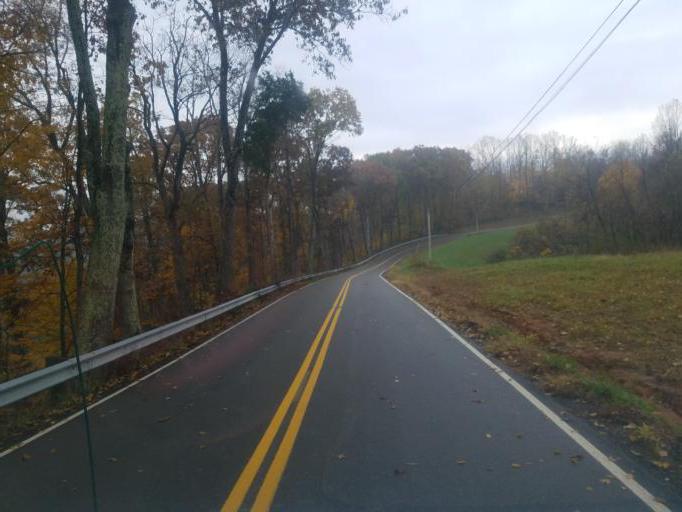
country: US
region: Ohio
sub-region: Morgan County
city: McConnelsville
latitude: 39.5682
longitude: -81.7847
